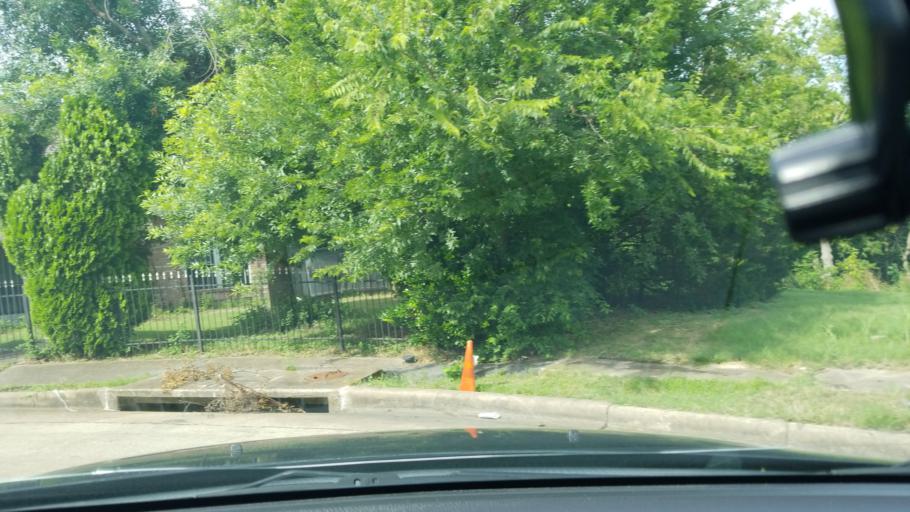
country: US
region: Texas
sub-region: Dallas County
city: Balch Springs
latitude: 32.7760
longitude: -96.6617
